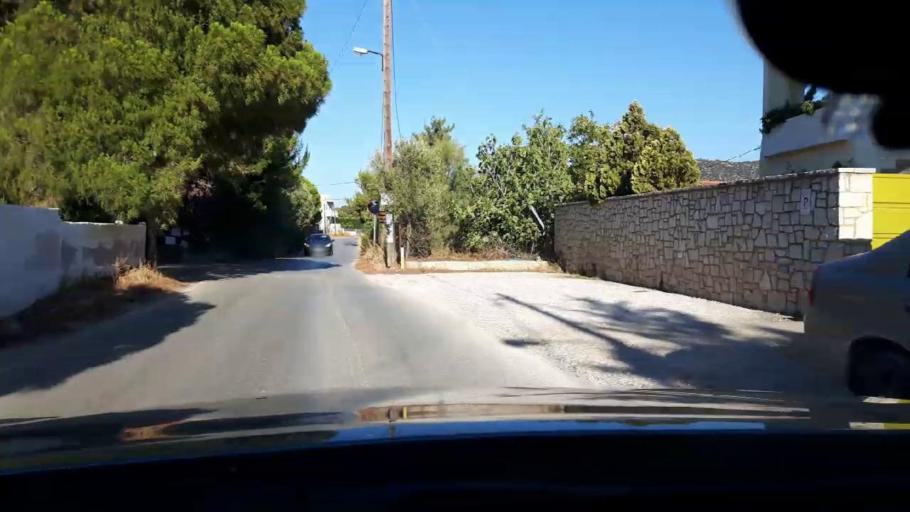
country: GR
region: Attica
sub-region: Nomarchia Anatolikis Attikis
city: Limin Mesoyaias
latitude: 37.8672
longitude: 24.0282
